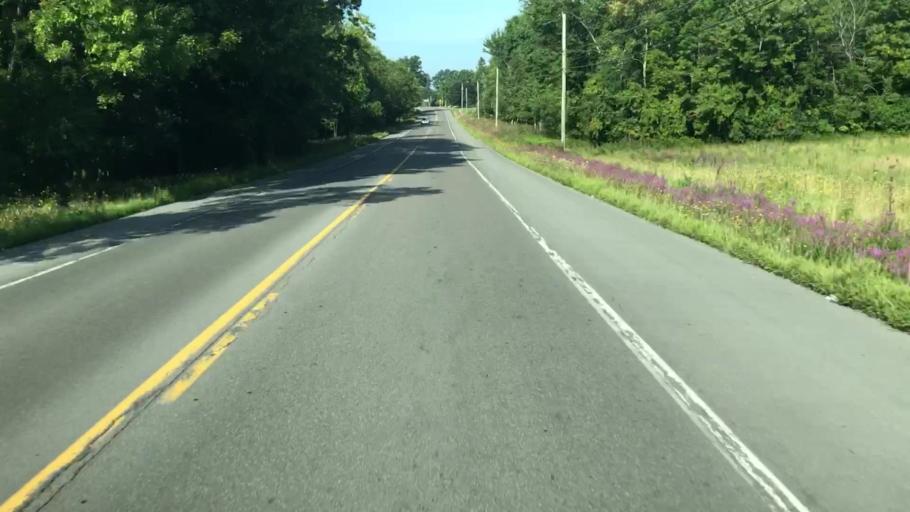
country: US
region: New York
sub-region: Onondaga County
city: Skaneateles
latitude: 42.9432
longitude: -76.4637
